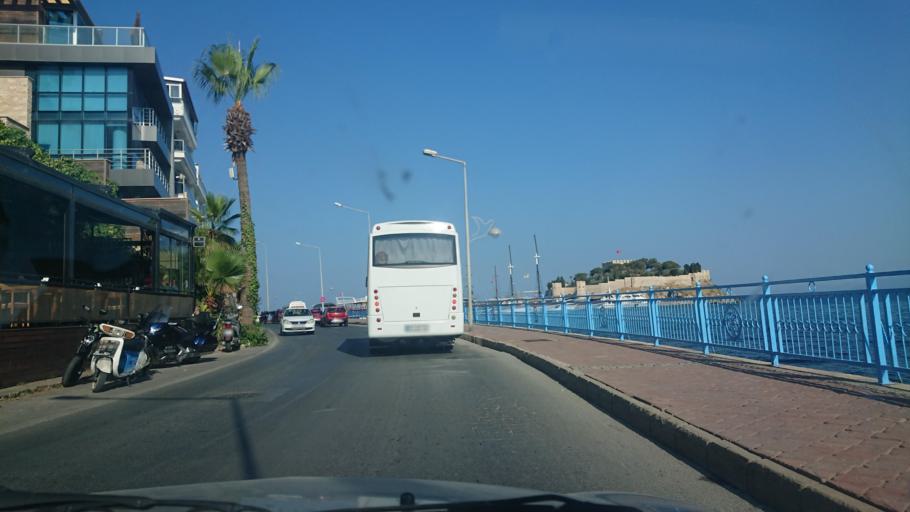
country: TR
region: Aydin
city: Kusadasi
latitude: 37.8612
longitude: 27.2519
